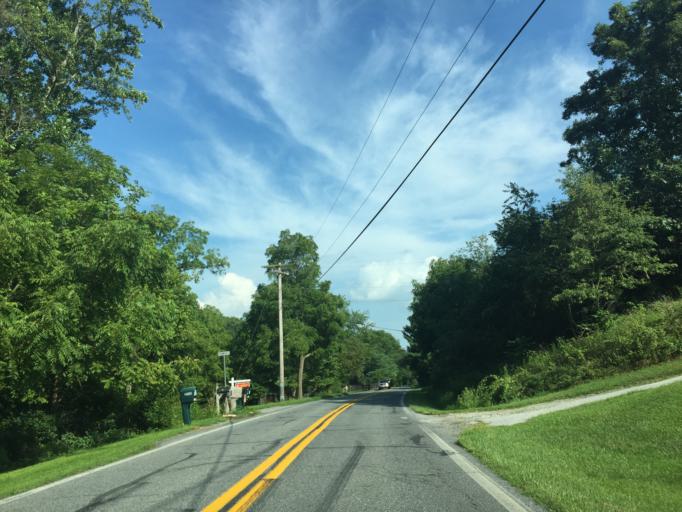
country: US
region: Maryland
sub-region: Carroll County
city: Manchester
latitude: 39.6296
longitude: -76.8965
